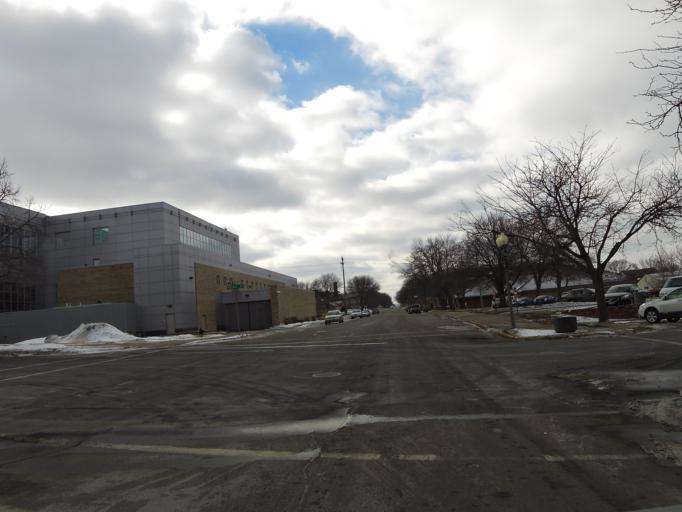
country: US
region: Minnesota
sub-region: Scott County
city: Shakopee
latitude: 44.7966
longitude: -93.5261
